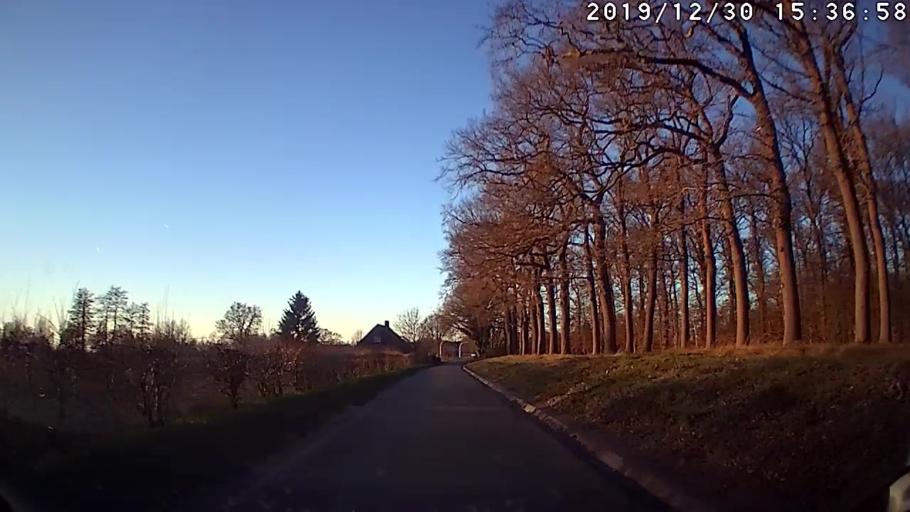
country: NL
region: Overijssel
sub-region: Gemeente Raalte
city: Heino
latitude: 52.4556
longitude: 6.1813
